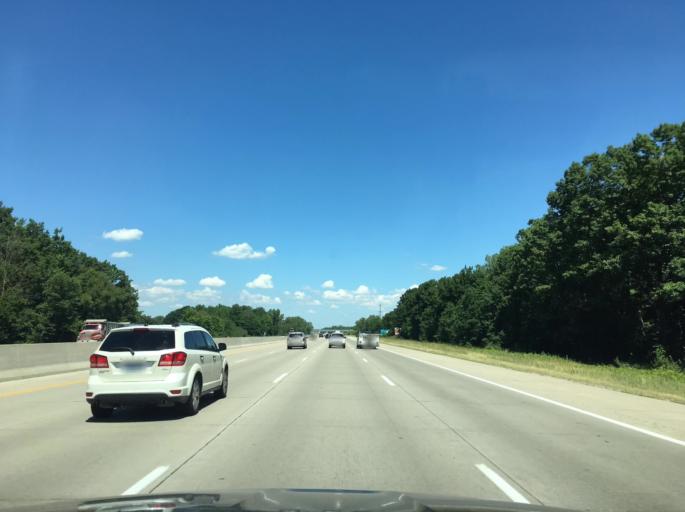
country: US
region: Michigan
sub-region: Saginaw County
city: Birch Run
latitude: 43.2875
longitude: -83.8134
